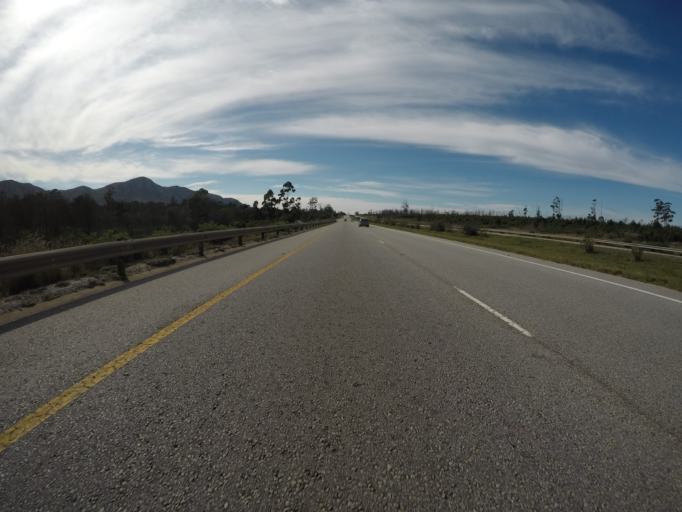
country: ZA
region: Eastern Cape
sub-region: Nelson Mandela Bay Metropolitan Municipality
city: Uitenhage
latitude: -33.9093
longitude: 25.2305
